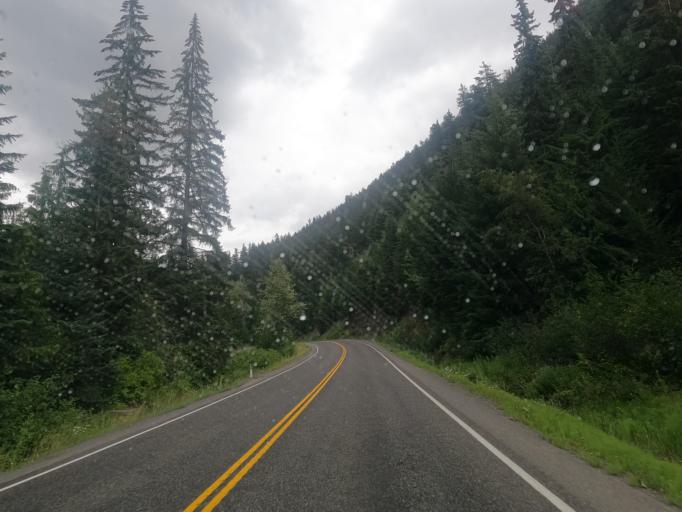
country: CA
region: British Columbia
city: Lillooet
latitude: 50.4782
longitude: -122.2180
